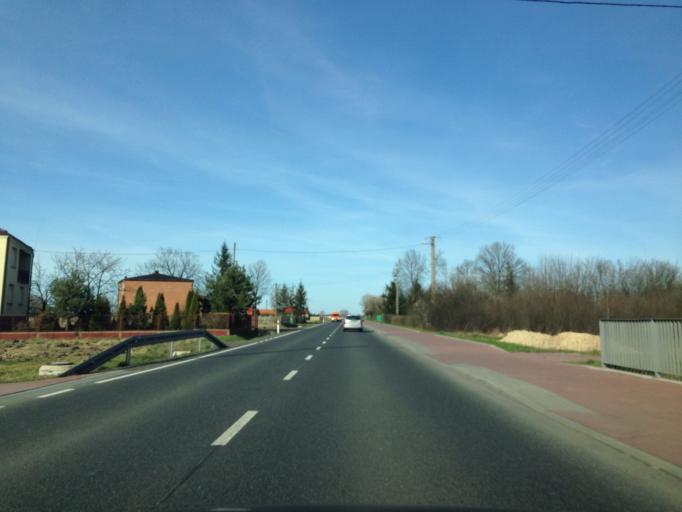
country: PL
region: Lodz Voivodeship
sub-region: Powiat poddebicki
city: Wartkowice
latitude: 51.9872
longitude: 19.0352
